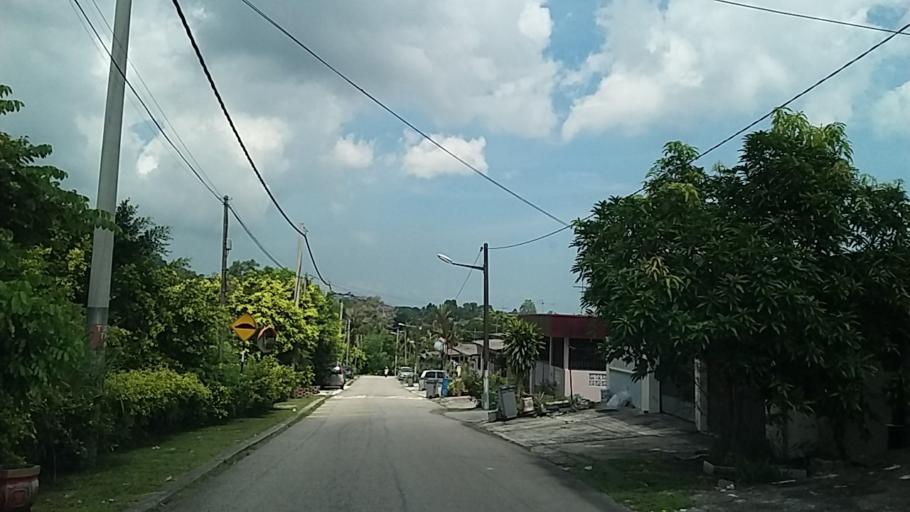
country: MY
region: Johor
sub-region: Daerah Batu Pahat
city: Batu Pahat
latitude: 1.8432
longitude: 102.9466
